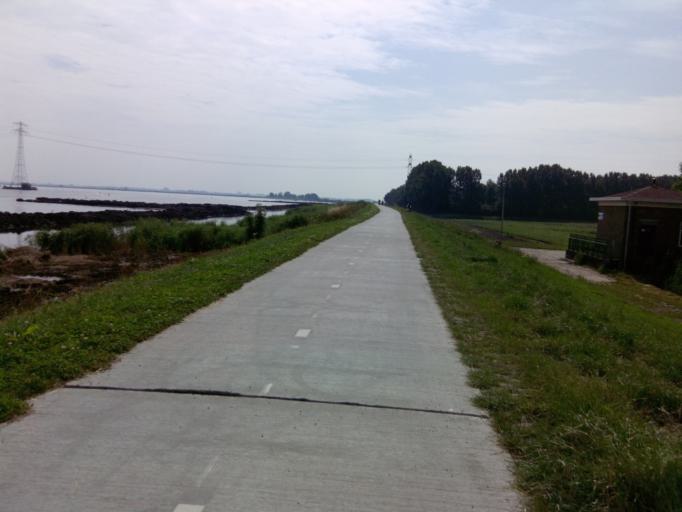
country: NL
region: Utrecht
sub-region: Gemeente Bunschoten
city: Bunschoten
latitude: 52.2528
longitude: 5.3884
